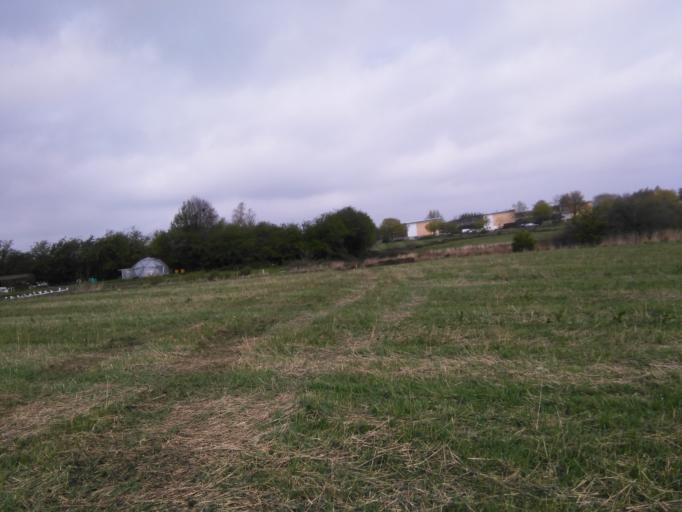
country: DK
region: Central Jutland
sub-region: Arhus Kommune
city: Beder
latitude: 56.0510
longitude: 10.2107
